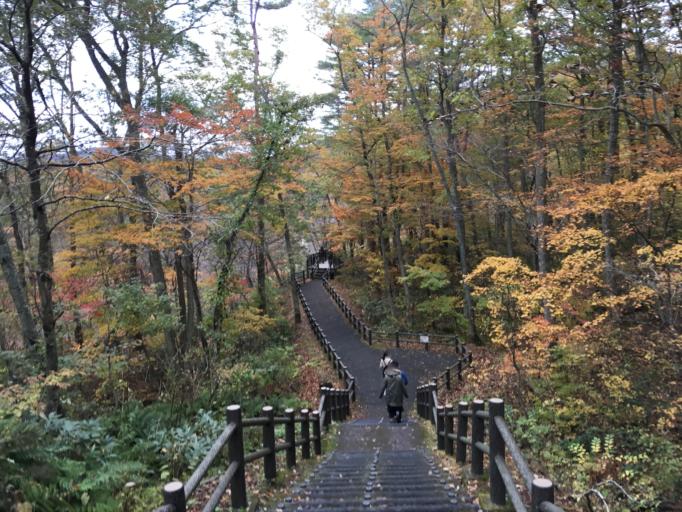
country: JP
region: Miyagi
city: Furukawa
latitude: 38.7317
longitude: 140.6890
